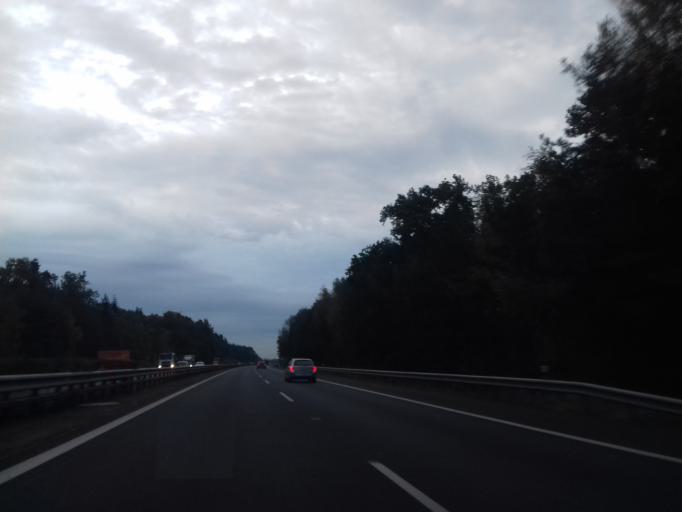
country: CZ
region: Central Bohemia
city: Poricany
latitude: 50.1247
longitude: 14.9232
